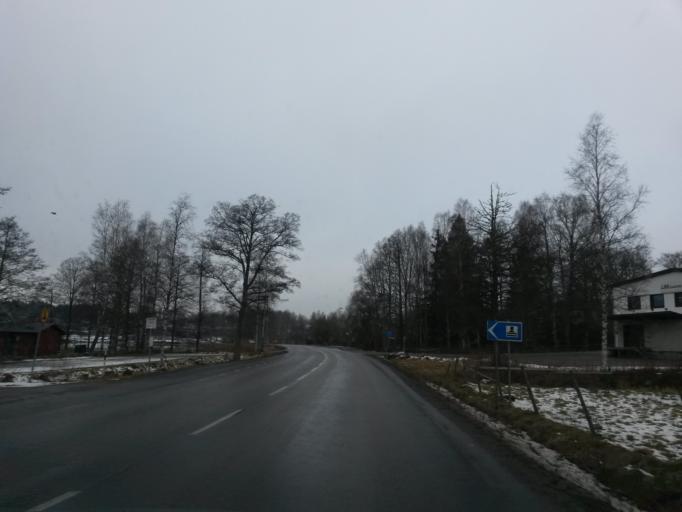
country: SE
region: Vaestra Goetaland
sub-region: Ulricehamns Kommun
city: Ulricehamn
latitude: 57.6787
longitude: 13.3851
